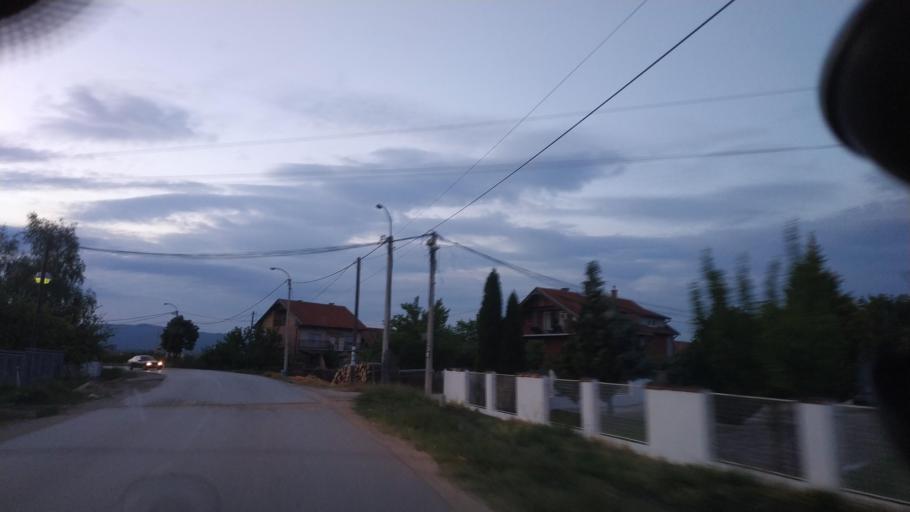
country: RS
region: Central Serbia
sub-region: Nisavski Okrug
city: Merosina
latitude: 43.2874
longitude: 21.7179
